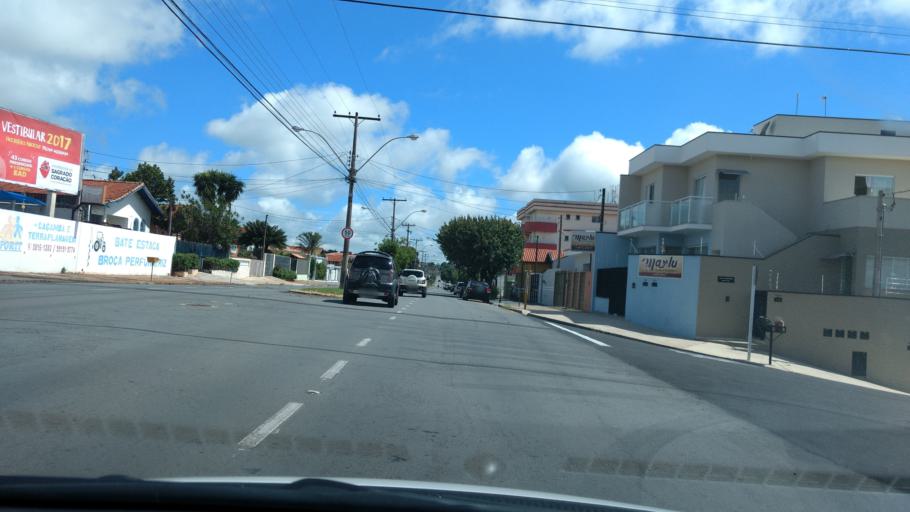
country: BR
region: Sao Paulo
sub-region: Botucatu
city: Botucatu
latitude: -22.8660
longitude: -48.4428
